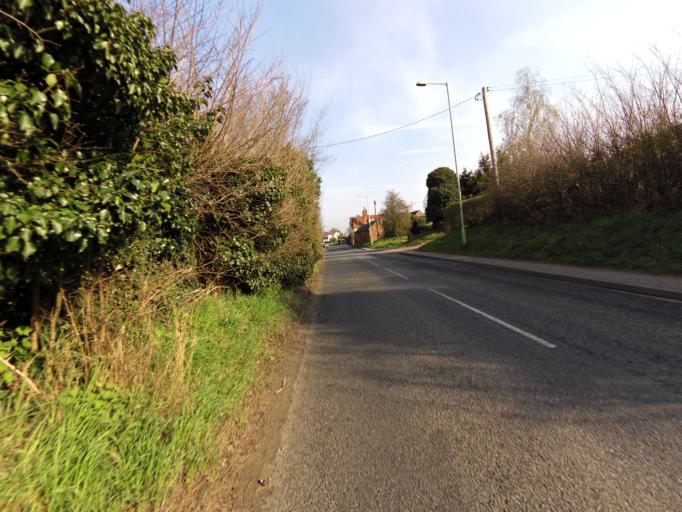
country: GB
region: England
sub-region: Suffolk
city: Bramford
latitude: 52.0751
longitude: 1.1071
